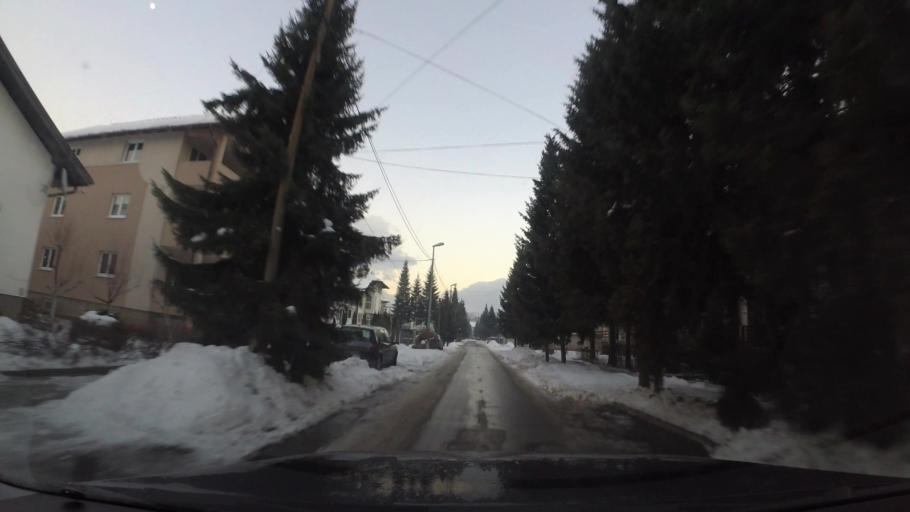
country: BA
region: Federation of Bosnia and Herzegovina
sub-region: Kanton Sarajevo
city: Sarajevo
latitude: 43.8290
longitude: 18.3002
